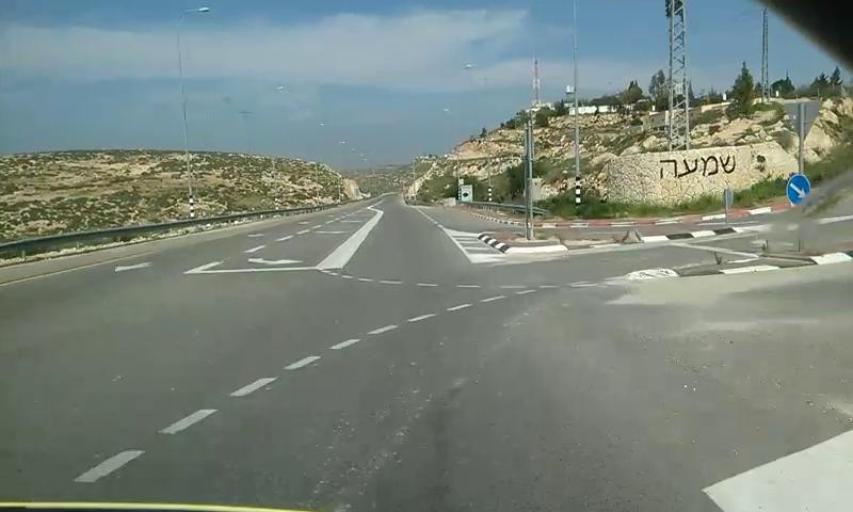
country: PS
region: West Bank
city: Az Zahiriyah
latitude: 31.3867
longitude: 35.0080
